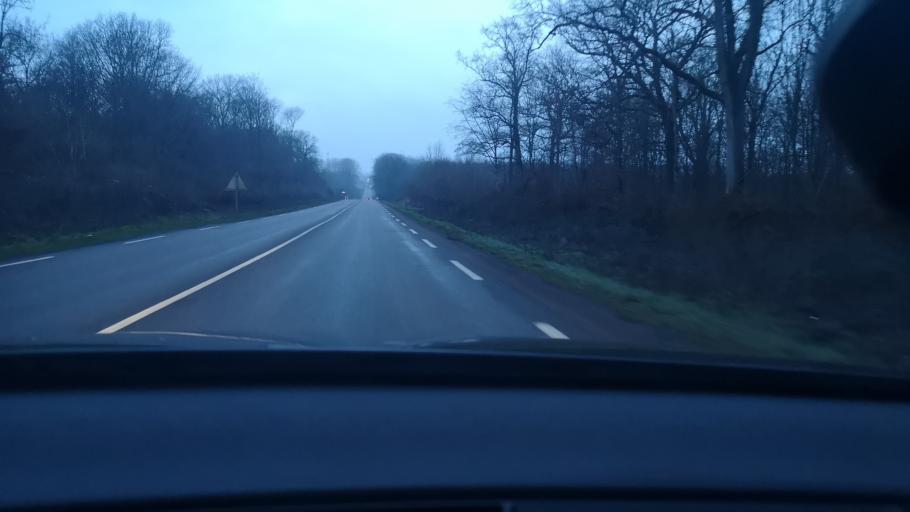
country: FR
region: Bourgogne
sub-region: Departement de Saone-et-Loire
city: Verdun-sur-le-Doubs
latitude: 47.0052
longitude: 5.0236
